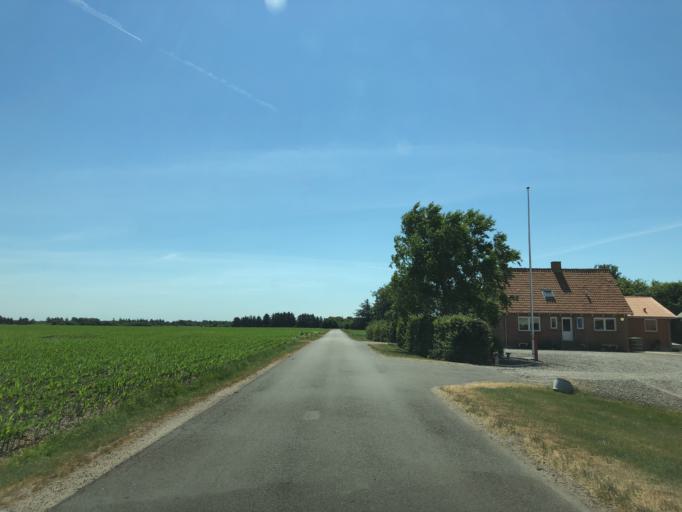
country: DK
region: Central Jutland
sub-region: Holstebro Kommune
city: Ulfborg
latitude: 56.3954
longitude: 8.4275
